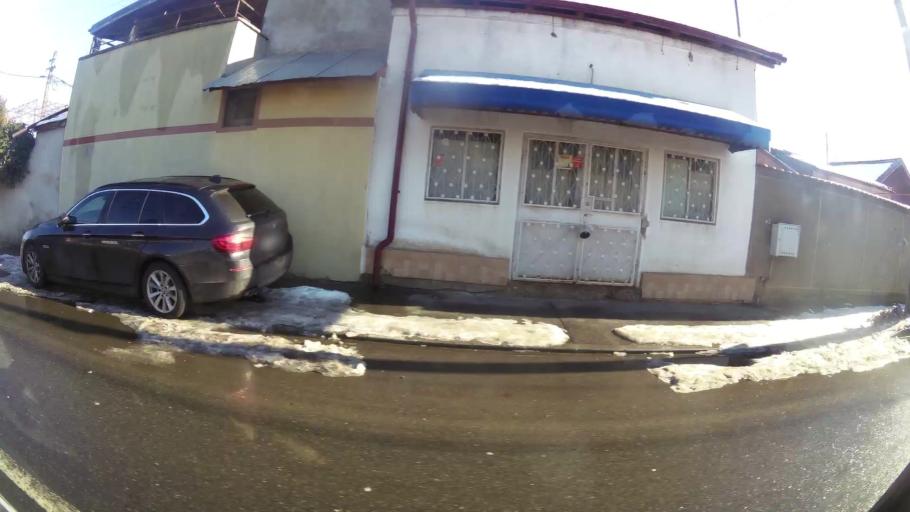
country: RO
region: Bucuresti
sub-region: Municipiul Bucuresti
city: Bucuresti
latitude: 44.4006
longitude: 26.0593
